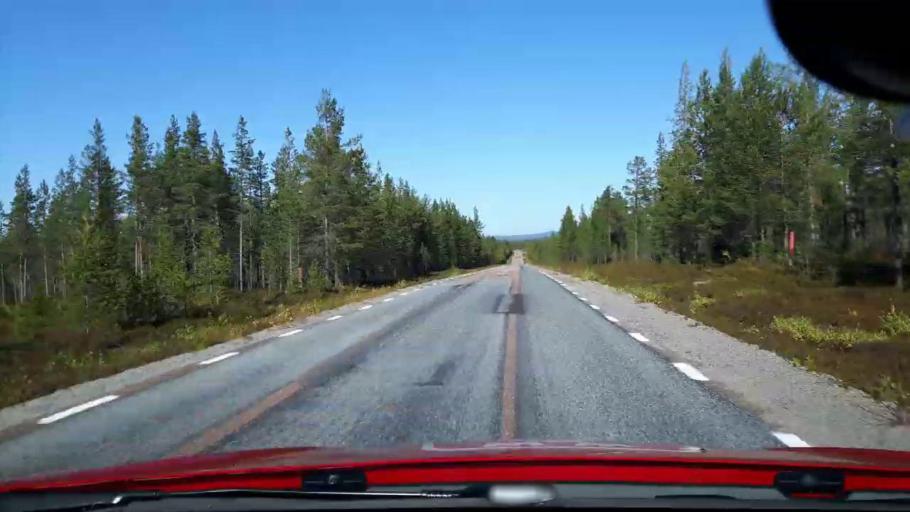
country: SE
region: Jaemtland
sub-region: Harjedalens Kommun
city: Sveg
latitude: 61.7315
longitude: 14.1647
